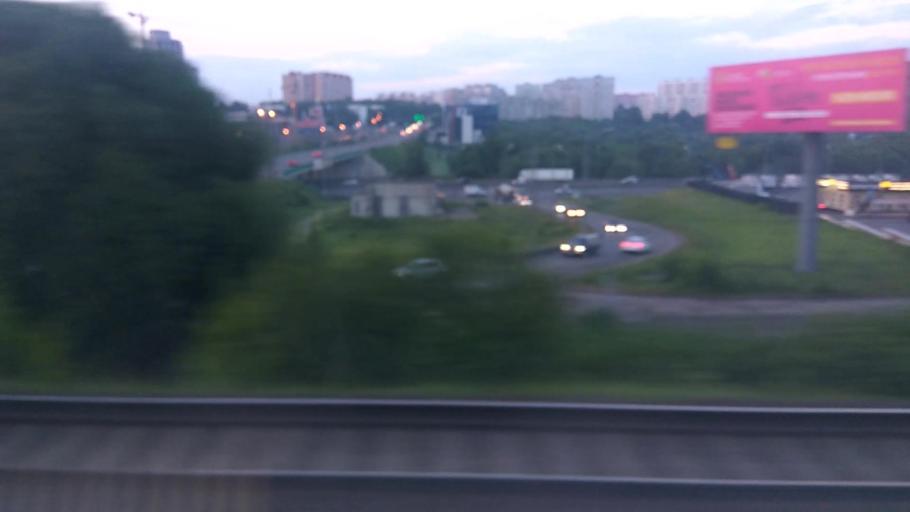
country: RU
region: Moskovskaya
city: Vidnoye
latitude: 55.5426
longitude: 37.6925
